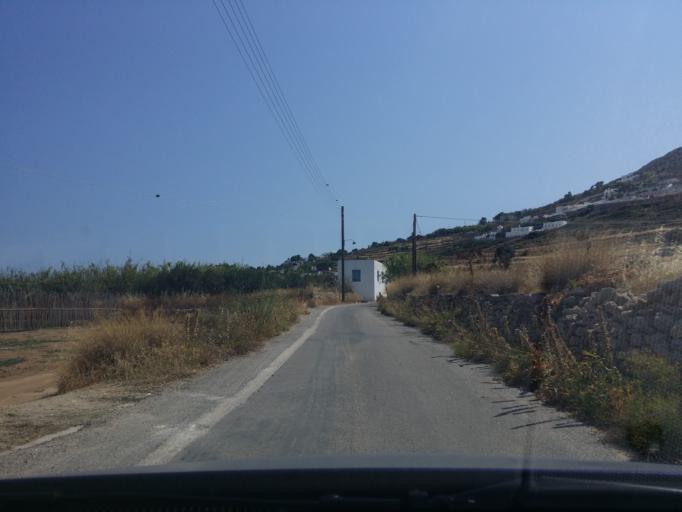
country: GR
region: South Aegean
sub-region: Nomos Kykladon
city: Antiparos
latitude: 37.0464
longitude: 25.1239
